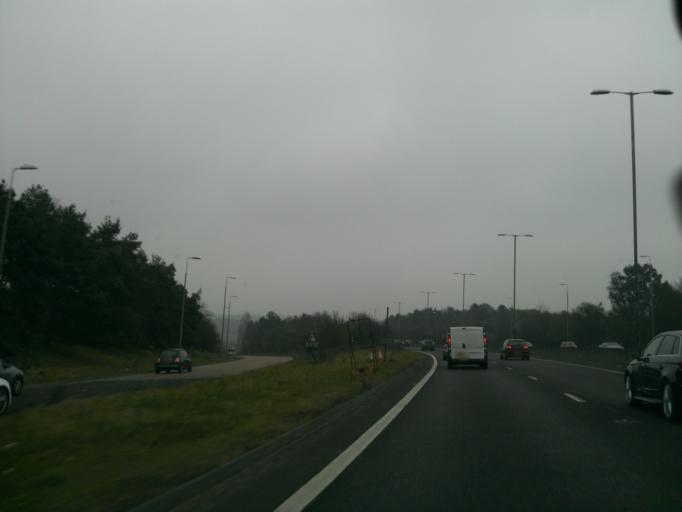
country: GB
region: England
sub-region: Essex
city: West Bergholt
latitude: 51.8922
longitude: 0.8486
